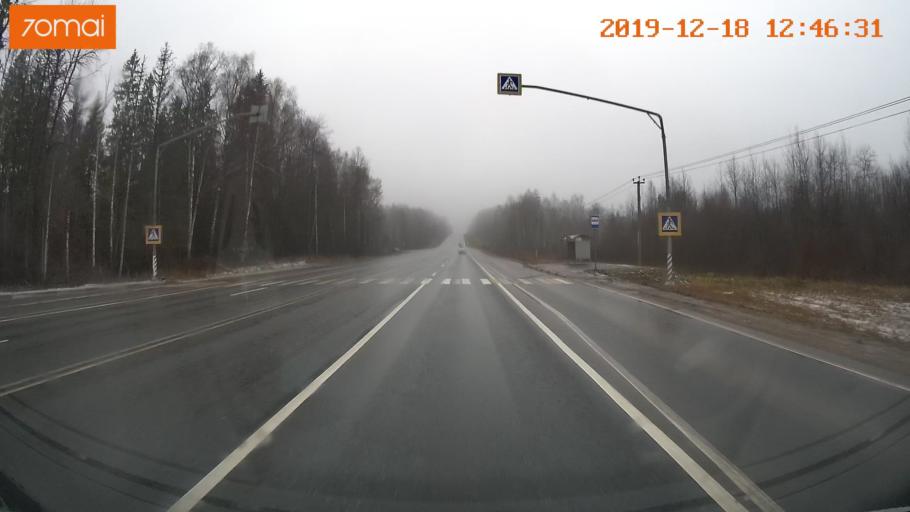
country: RU
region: Moskovskaya
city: Klin
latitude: 56.2446
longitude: 36.6656
